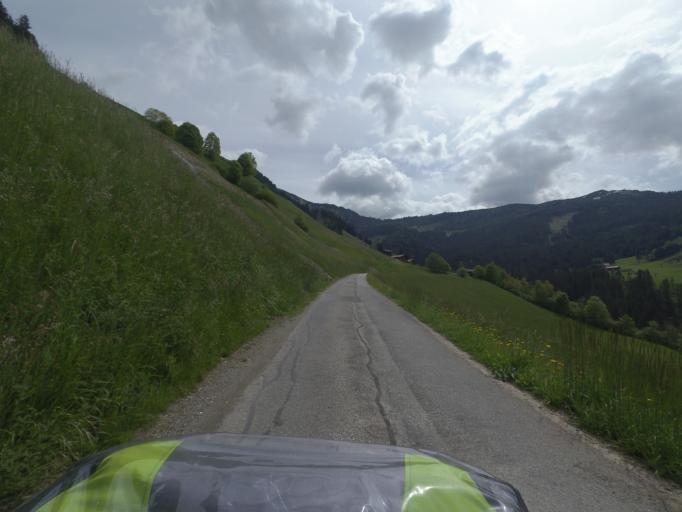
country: AT
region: Salzburg
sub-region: Politischer Bezirk Sankt Johann im Pongau
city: Dorfgastein
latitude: 47.2527
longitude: 13.1211
